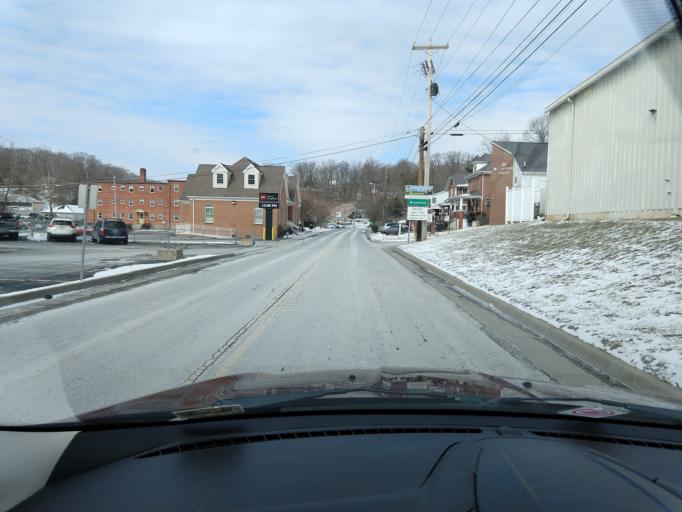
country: US
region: West Virginia
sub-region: Mercer County
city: Bluefield
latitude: 37.2448
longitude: -81.2401
